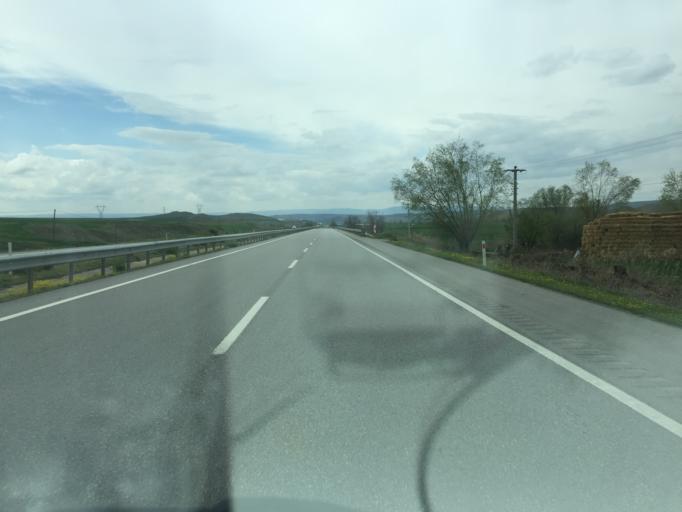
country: TR
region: Corum
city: Sungurlu
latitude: 40.1426
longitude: 34.2744
